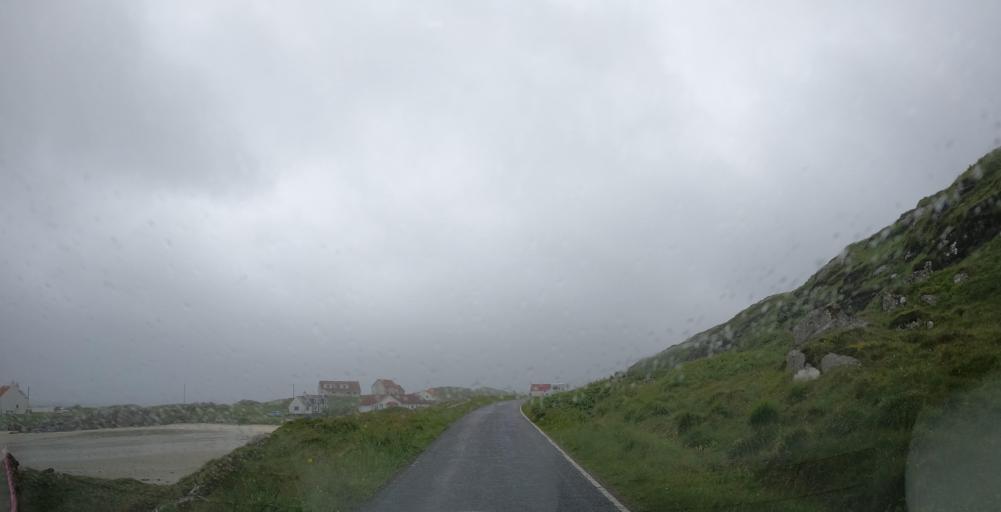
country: GB
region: Scotland
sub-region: Eilean Siar
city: Barra
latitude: 57.0153
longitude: -7.4328
